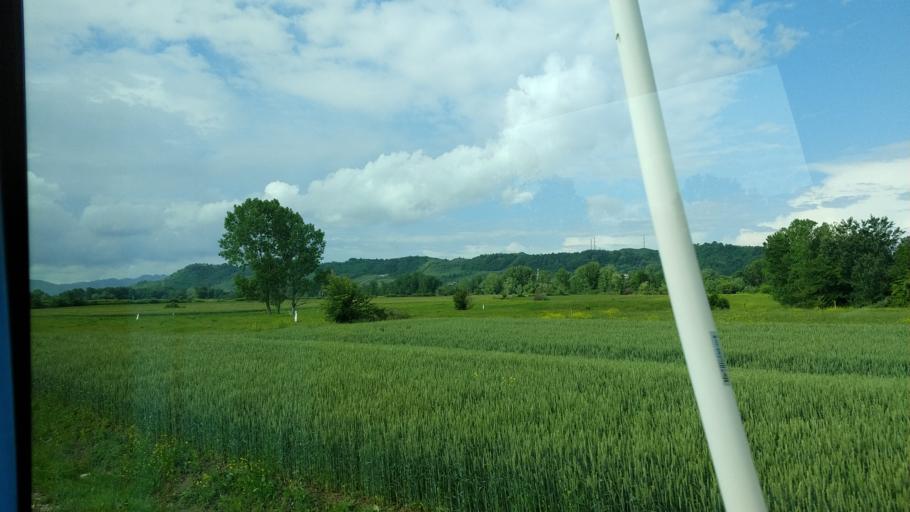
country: AL
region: Tirane
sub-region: Rrethi i Tiranes
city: Berxull
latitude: 41.4092
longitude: 19.7036
